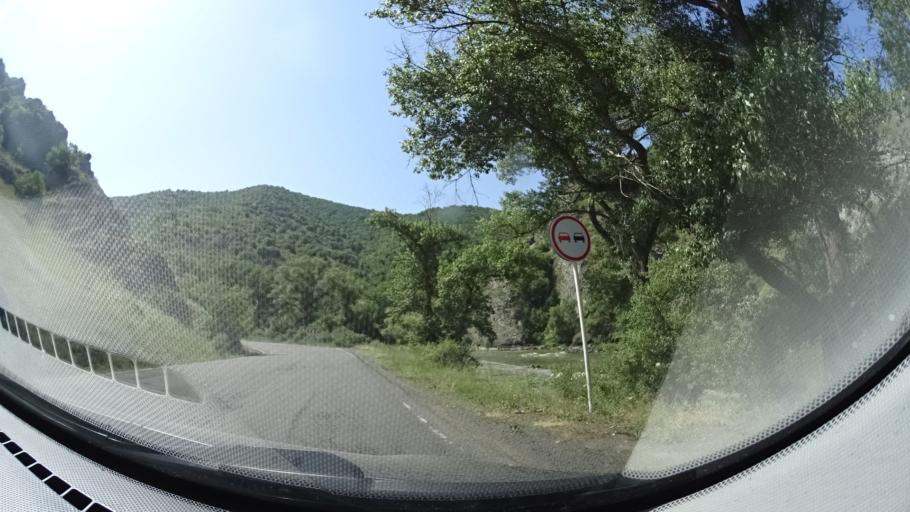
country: GE
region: Samtskhe-Javakheti
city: Akhaltsikhe
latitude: 41.6208
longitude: 43.0493
